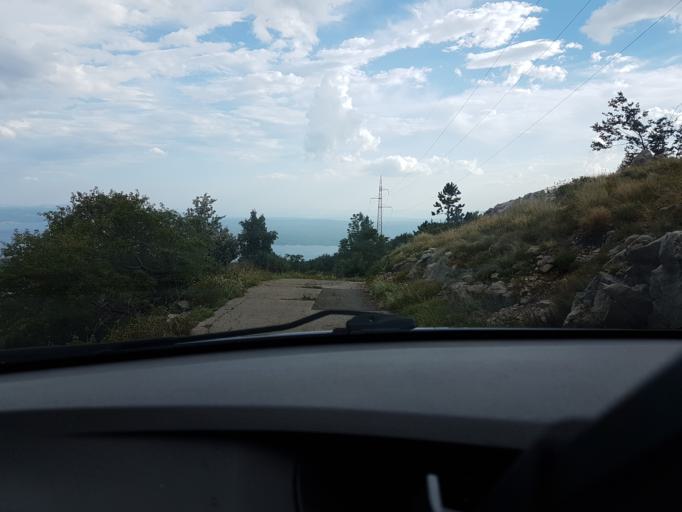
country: HR
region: Primorsko-Goranska
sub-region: Grad Crikvenica
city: Crikvenica
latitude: 45.2430
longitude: 14.6889
